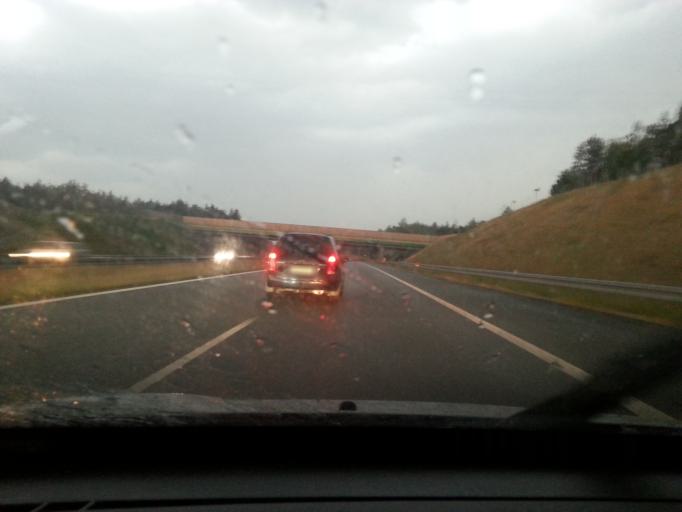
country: PL
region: Lodz Voivodeship
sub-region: powiat Lowicki
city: Lyszkowice
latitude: 51.9606
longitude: 19.8506
